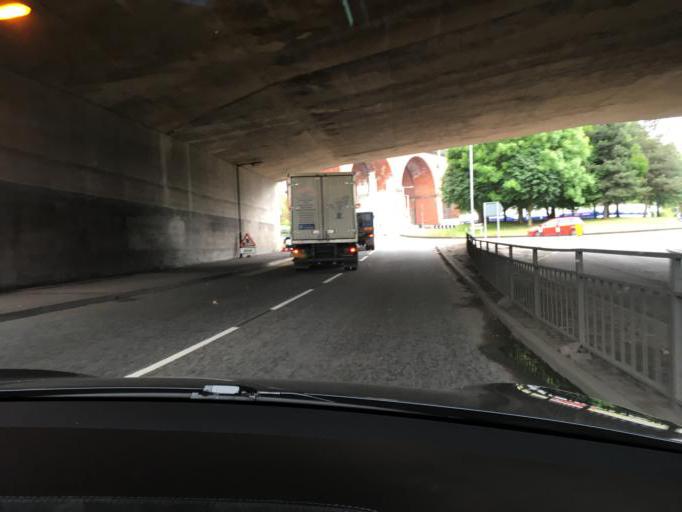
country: GB
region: England
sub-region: Borough of Stockport
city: Stockport
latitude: 53.4104
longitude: -2.1679
